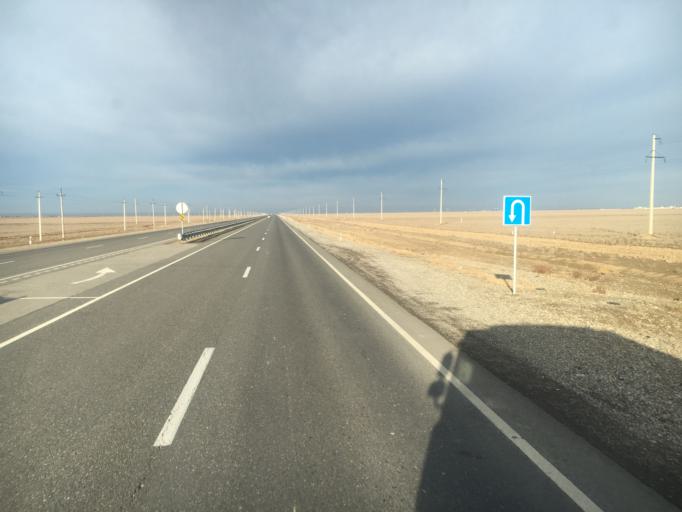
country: KZ
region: Ongtustik Qazaqstan
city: Turkestan
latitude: 43.4296
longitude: 67.9935
